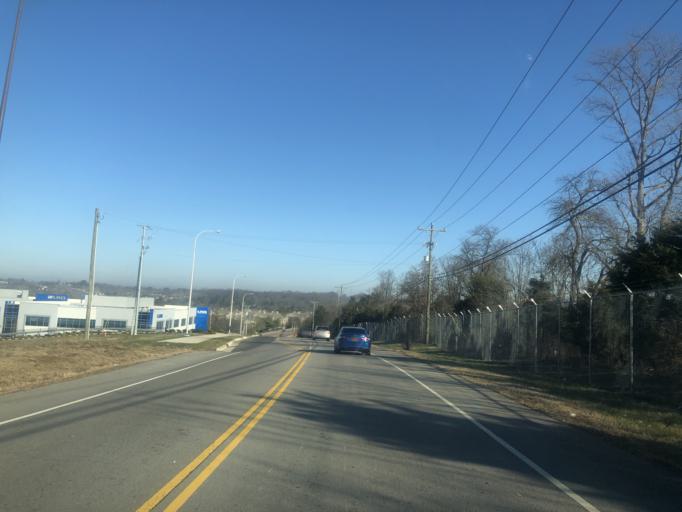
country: US
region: Tennessee
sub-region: Rutherford County
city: La Vergne
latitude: 36.0327
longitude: -86.6388
